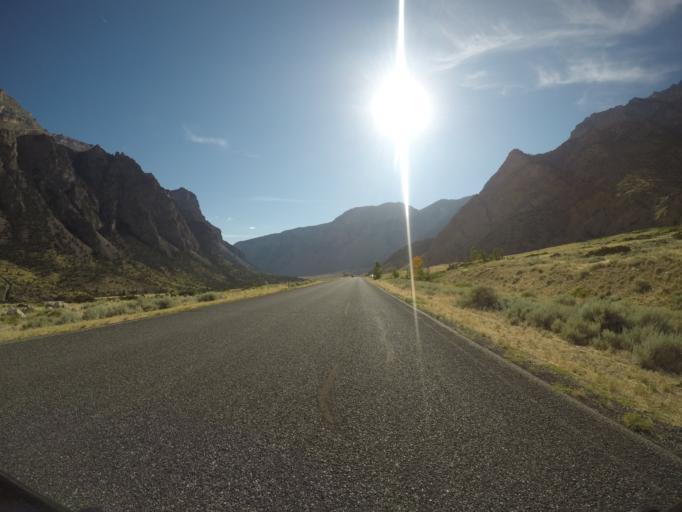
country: US
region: Montana
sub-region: Carbon County
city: Red Lodge
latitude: 44.8457
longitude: -109.3127
